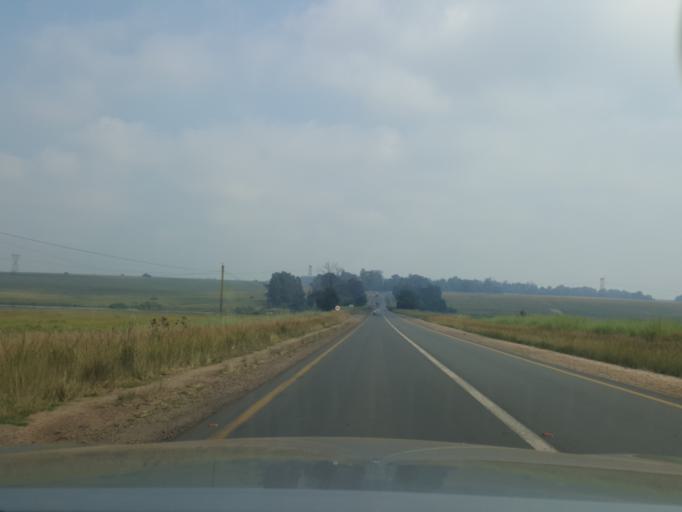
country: ZA
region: Mpumalanga
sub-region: Nkangala District Municipality
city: Witbank
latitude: -26.0042
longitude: 29.2945
